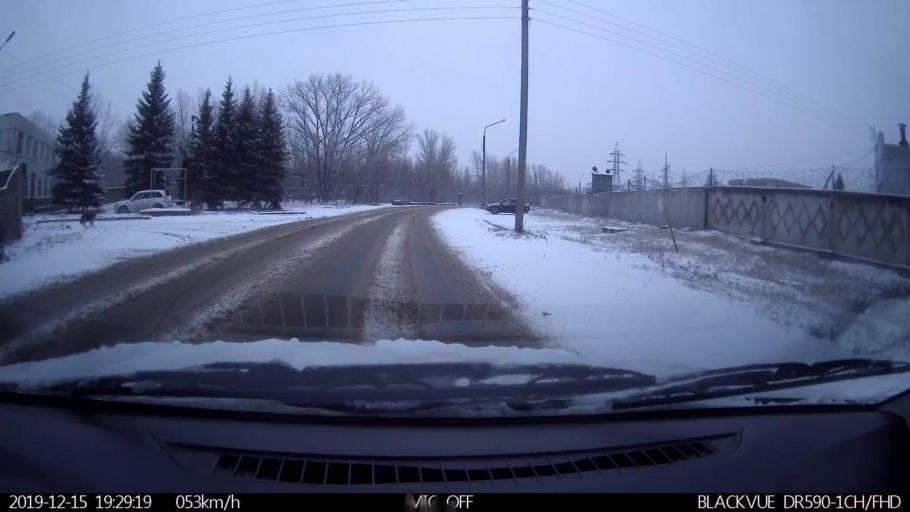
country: RU
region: Nizjnij Novgorod
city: Neklyudovo
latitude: 56.3544
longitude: 43.8949
